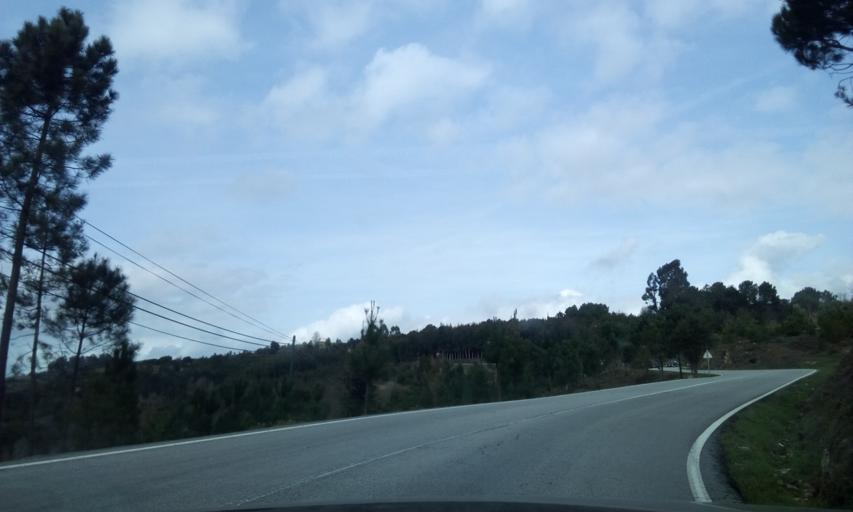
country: PT
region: Viseu
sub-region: Satao
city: Satao
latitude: 40.6664
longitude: -7.6838
